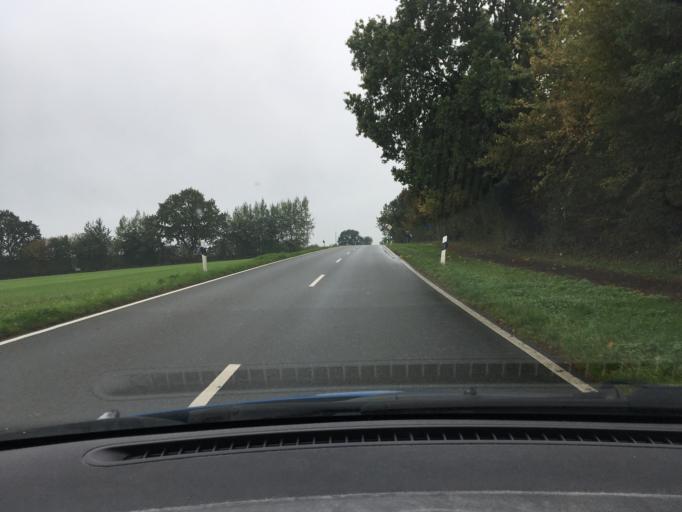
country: DE
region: Schleswig-Holstein
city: Bosdorf
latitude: 54.1086
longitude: 10.4797
